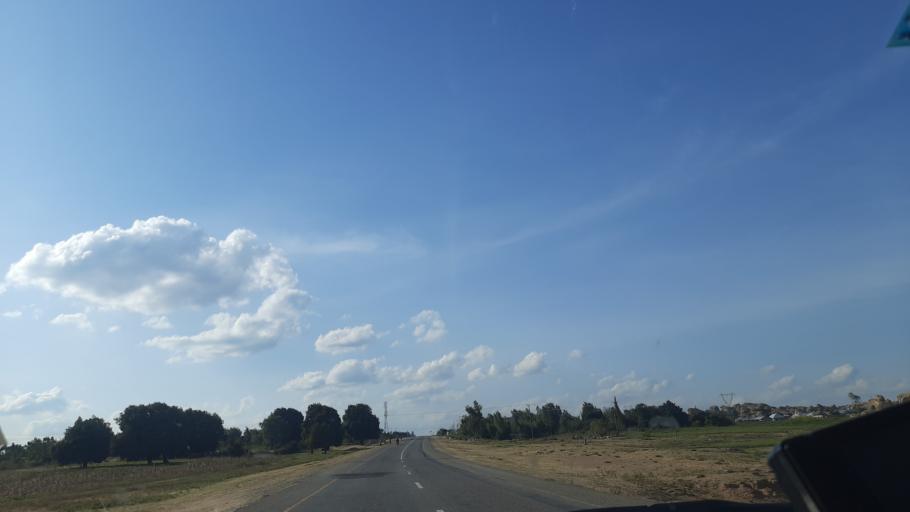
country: TZ
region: Singida
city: Puma
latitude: -5.0113
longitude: 34.7575
